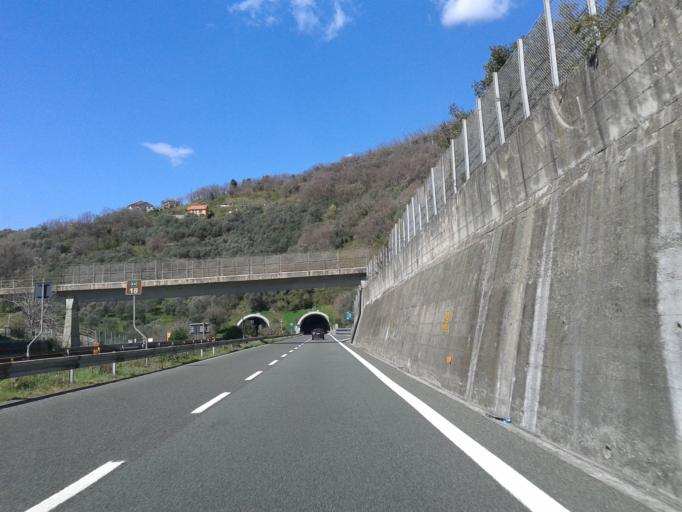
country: IT
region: Liguria
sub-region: Provincia di Genova
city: Moneglia
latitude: 44.2545
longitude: 9.5064
